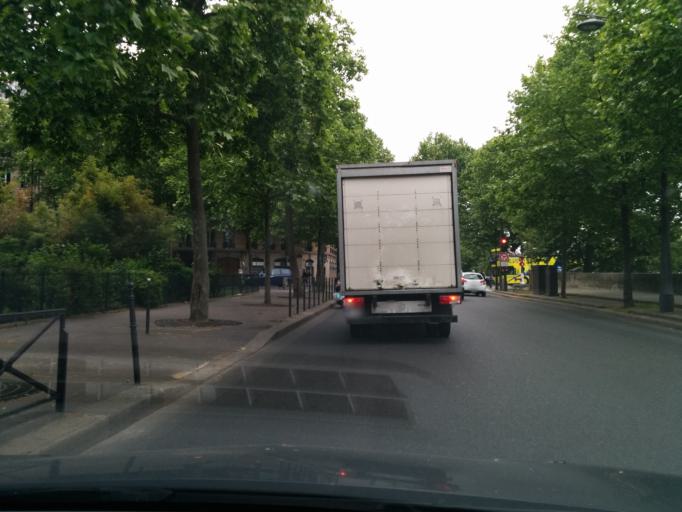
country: FR
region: Ile-de-France
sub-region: Paris
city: Paris
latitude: 48.8514
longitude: 2.3615
